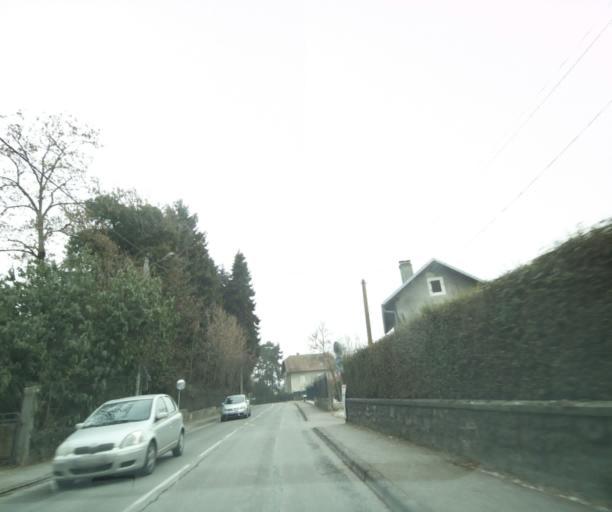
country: FR
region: Rhone-Alpes
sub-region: Departement de la Haute-Savoie
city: Reignier-Esery
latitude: 46.1274
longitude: 6.2664
